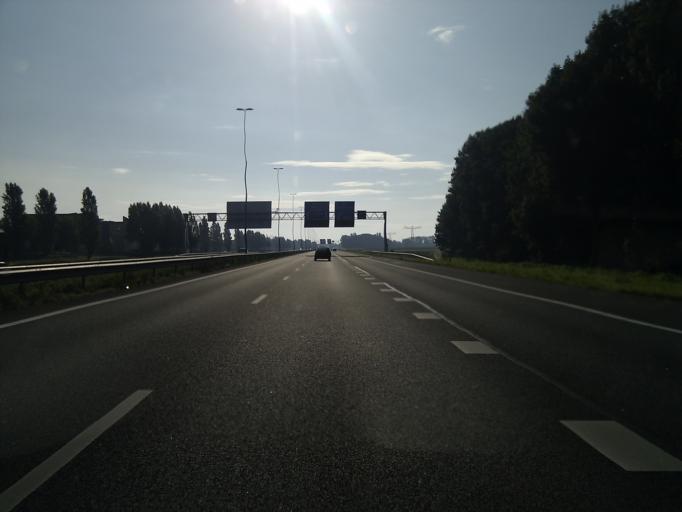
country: NL
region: Gelderland
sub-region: Gemeente Beuningen
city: Beuningen
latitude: 51.8541
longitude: 5.7305
